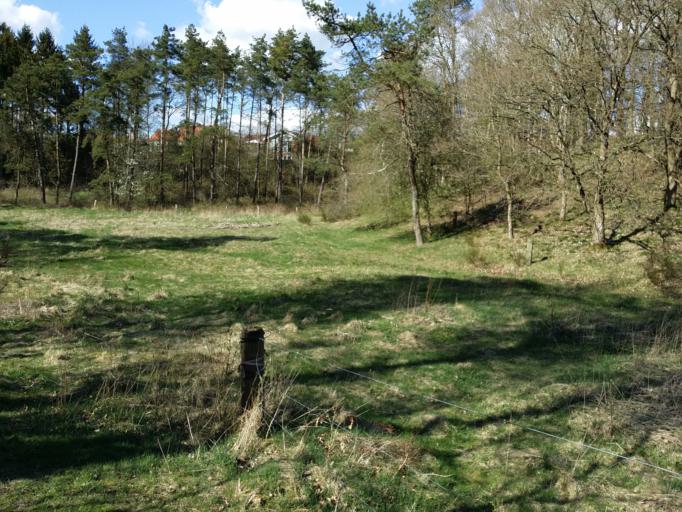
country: DK
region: Central Jutland
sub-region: Skanderborg Kommune
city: Ry
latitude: 56.0787
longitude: 9.7754
